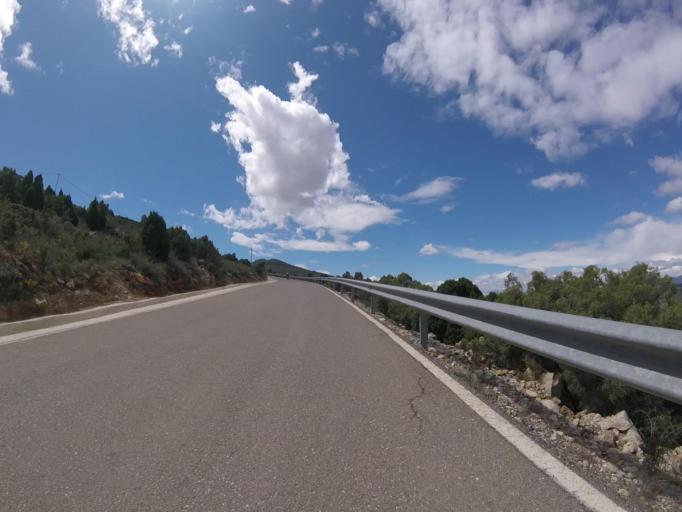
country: ES
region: Valencia
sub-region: Provincia de Castello
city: Sierra-Engarceran
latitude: 40.2922
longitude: -0.0369
